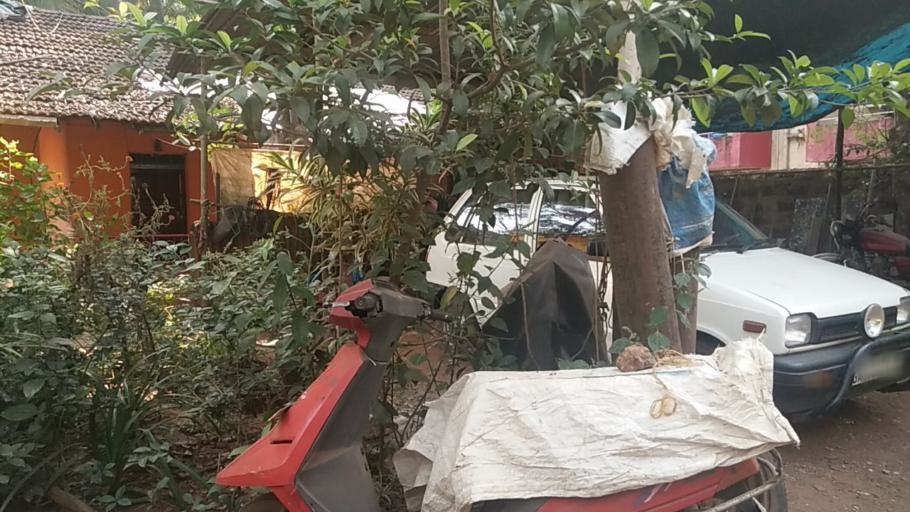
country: IN
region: Goa
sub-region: South Goa
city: Varca
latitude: 15.2396
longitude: 73.9450
